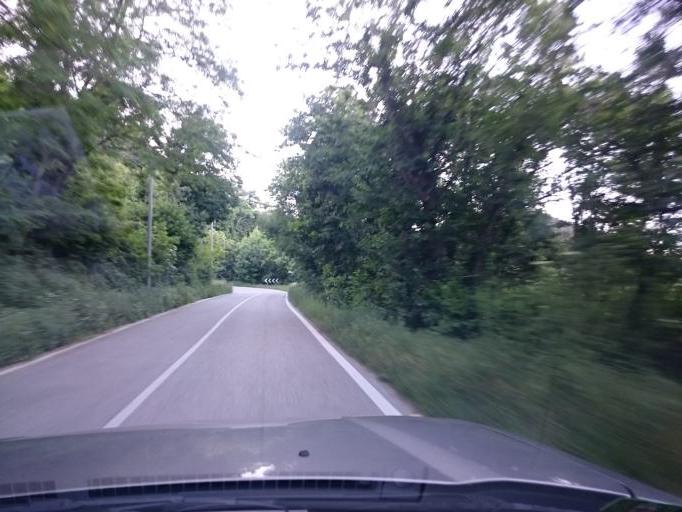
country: IT
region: Veneto
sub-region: Provincia di Padova
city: Torreglia
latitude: 45.3294
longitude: 11.7000
